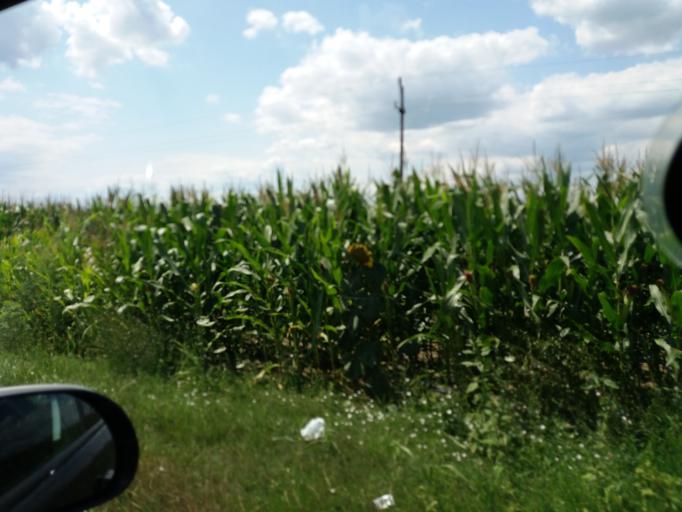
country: RS
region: Autonomna Pokrajina Vojvodina
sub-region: Sremski Okrug
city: Pecinci
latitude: 44.8959
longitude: 19.9662
